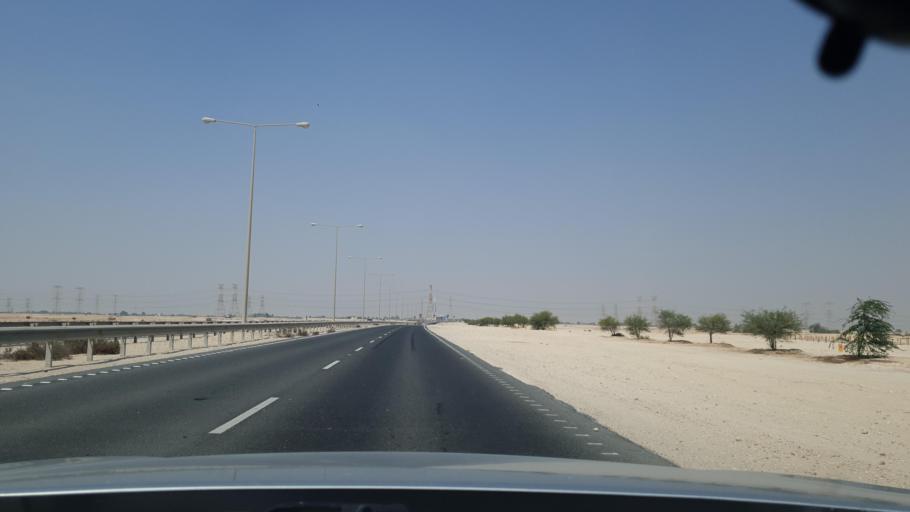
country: QA
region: Al Khawr
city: Al Khawr
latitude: 25.7472
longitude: 51.4807
